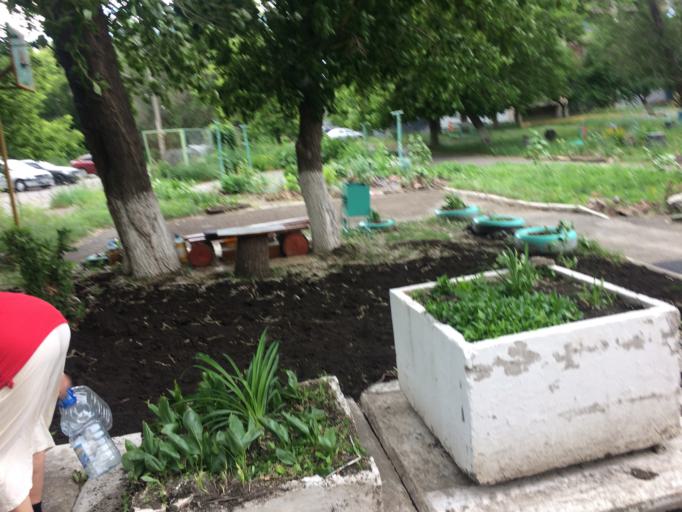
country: RU
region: Chelyabinsk
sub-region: Gorod Magnitogorsk
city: Magnitogorsk
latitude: 53.4105
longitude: 58.9801
